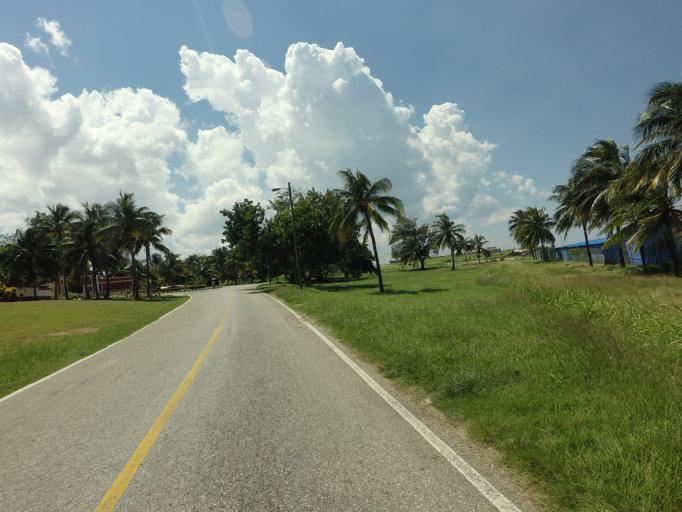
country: CU
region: La Habana
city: Centro Habana
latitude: 23.1526
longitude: -82.3511
